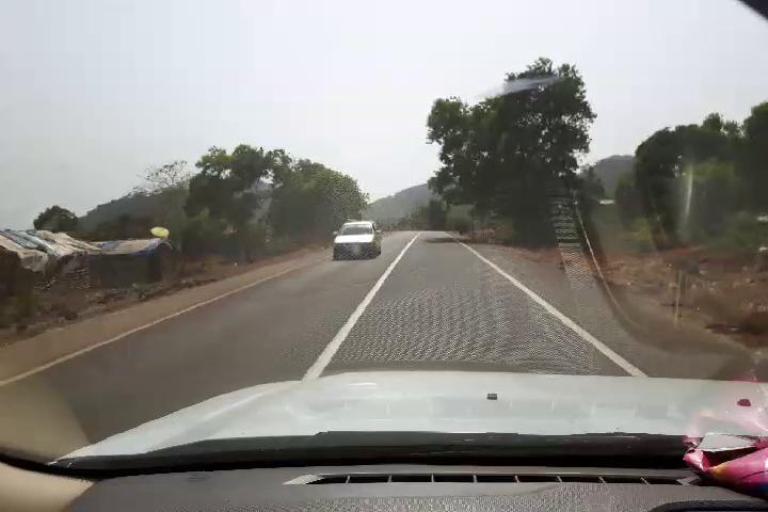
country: SL
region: Western Area
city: Waterloo
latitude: 8.2036
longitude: -13.1283
